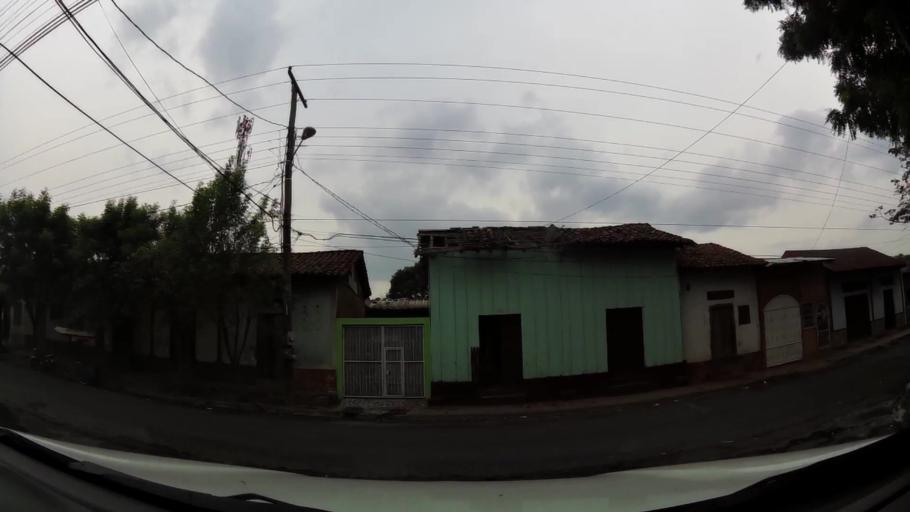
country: NI
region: Leon
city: Leon
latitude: 12.4445
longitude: -86.8797
